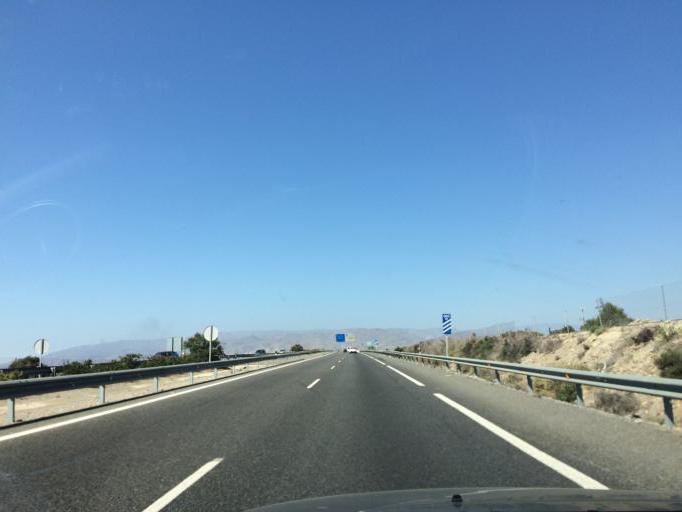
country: ES
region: Andalusia
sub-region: Provincia de Almeria
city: Viator
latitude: 36.8838
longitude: -2.3680
